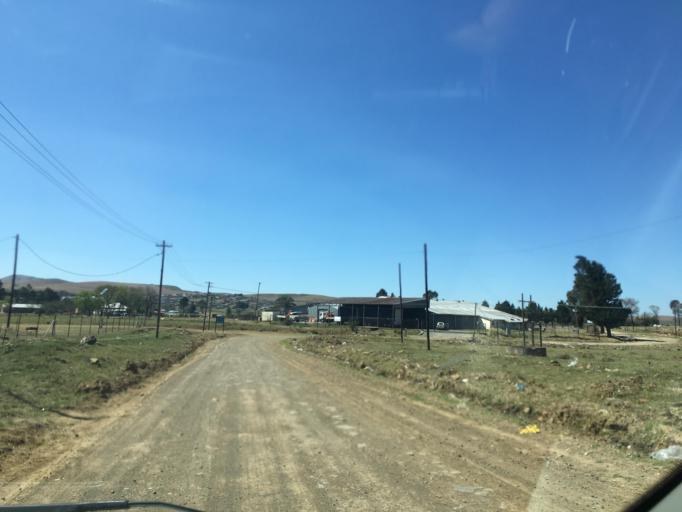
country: ZA
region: Eastern Cape
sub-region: Chris Hani District Municipality
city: Elliot
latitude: -31.3393
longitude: 27.8415
